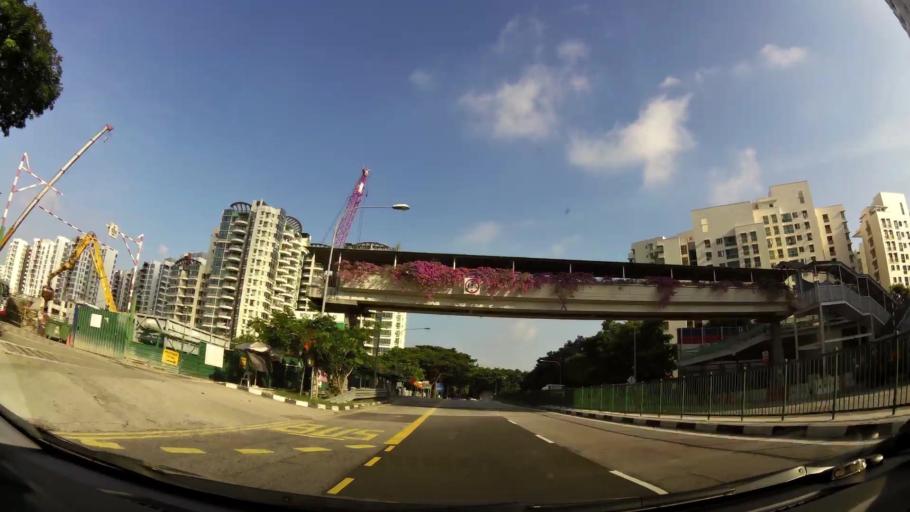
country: SG
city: Singapore
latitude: 1.3361
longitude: 103.9333
